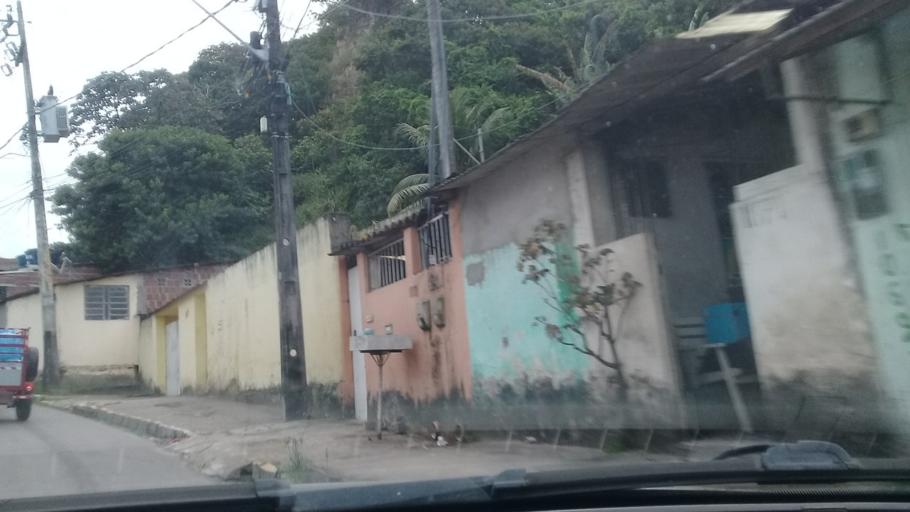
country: BR
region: Pernambuco
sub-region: Jaboatao Dos Guararapes
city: Jaboatao
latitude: -8.1375
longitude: -34.9441
